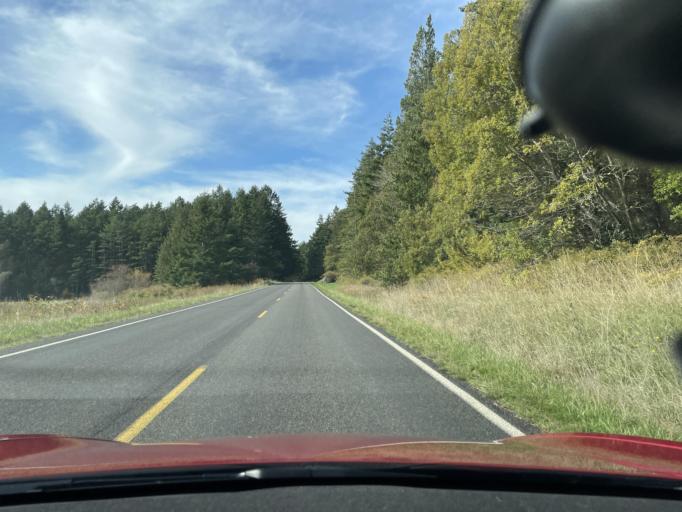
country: US
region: Washington
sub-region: San Juan County
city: Friday Harbor
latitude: 48.5290
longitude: -122.9852
